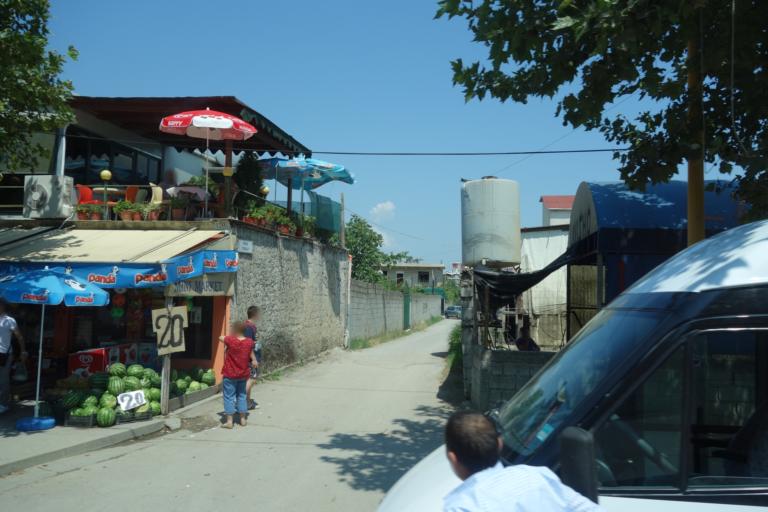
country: AL
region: Tirane
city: Tirana
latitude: 41.3189
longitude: 19.7805
